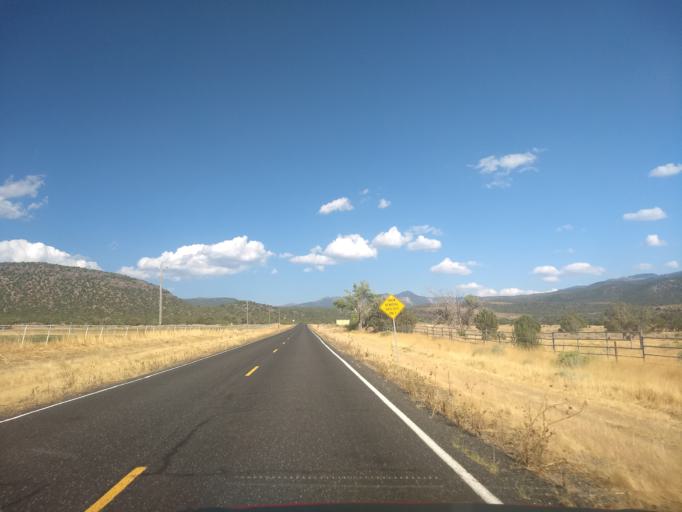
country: US
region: Utah
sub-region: Washington County
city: Enterprise
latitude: 37.4170
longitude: -113.6149
